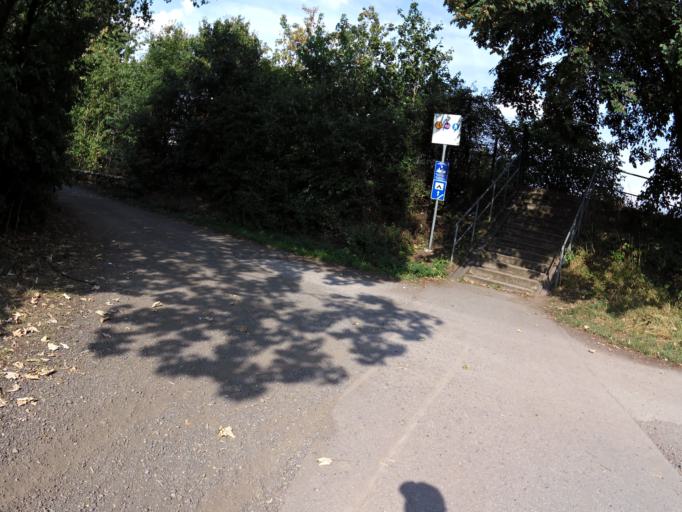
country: DE
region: North Rhine-Westphalia
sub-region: Regierungsbezirk Detmold
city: Petershagen
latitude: 52.3669
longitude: 8.9785
